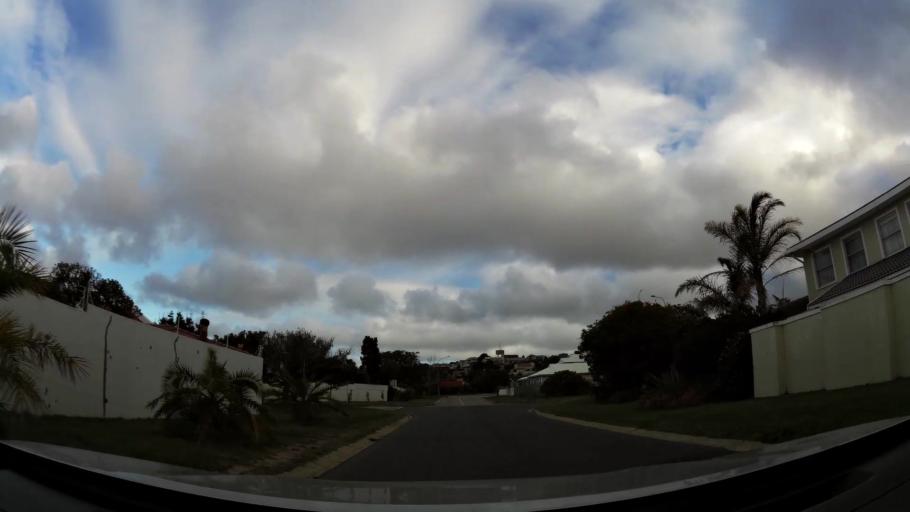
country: ZA
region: Western Cape
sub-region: Eden District Municipality
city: Plettenberg Bay
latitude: -34.0493
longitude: 23.3638
